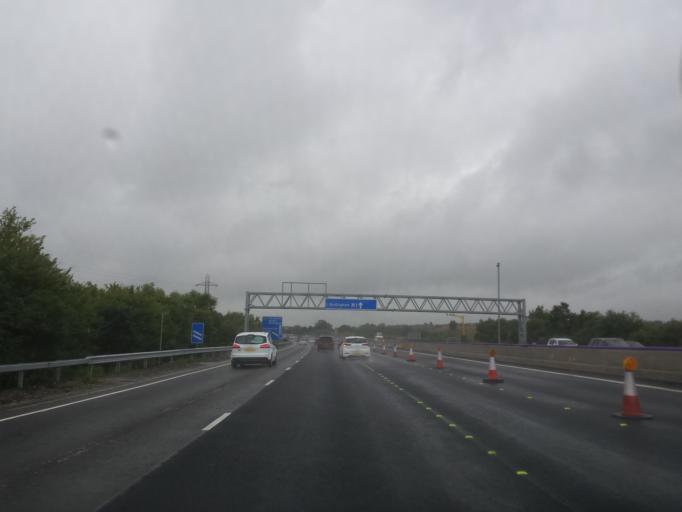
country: GB
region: England
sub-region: Derbyshire
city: Staveley
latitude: 53.2532
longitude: -1.3250
